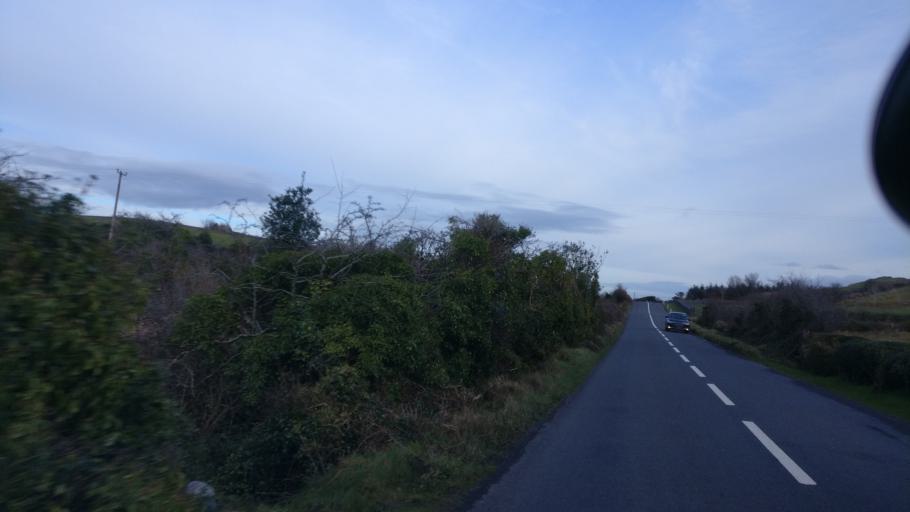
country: IE
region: Connaught
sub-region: County Galway
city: Oughterard
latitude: 53.5317
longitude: -9.3401
